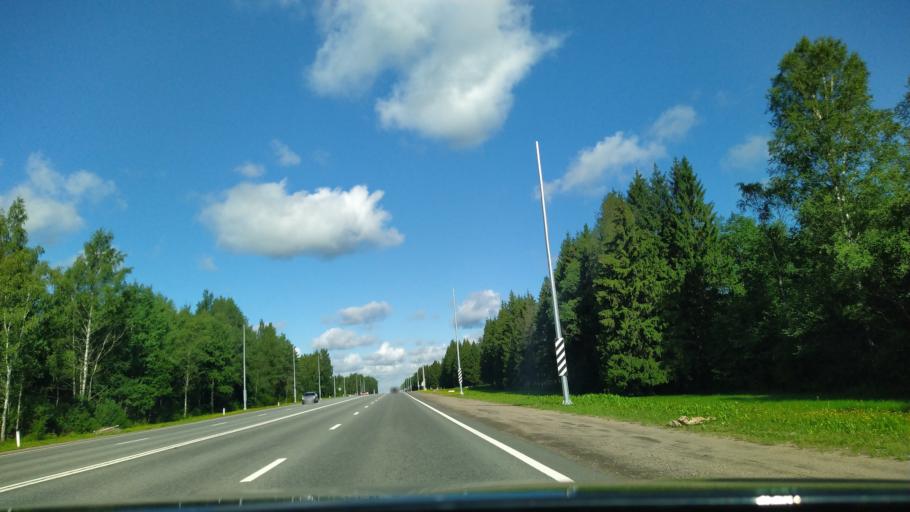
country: RU
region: Leningrad
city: Ul'yanovka
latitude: 59.5883
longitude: 30.7912
